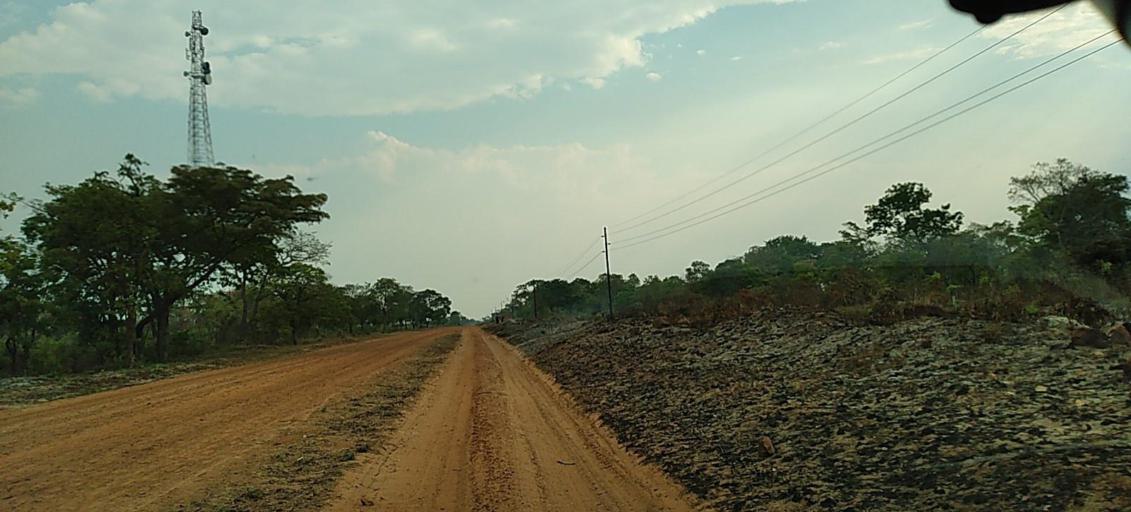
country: ZM
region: North-Western
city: Kabompo
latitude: -13.8846
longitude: 23.6623
